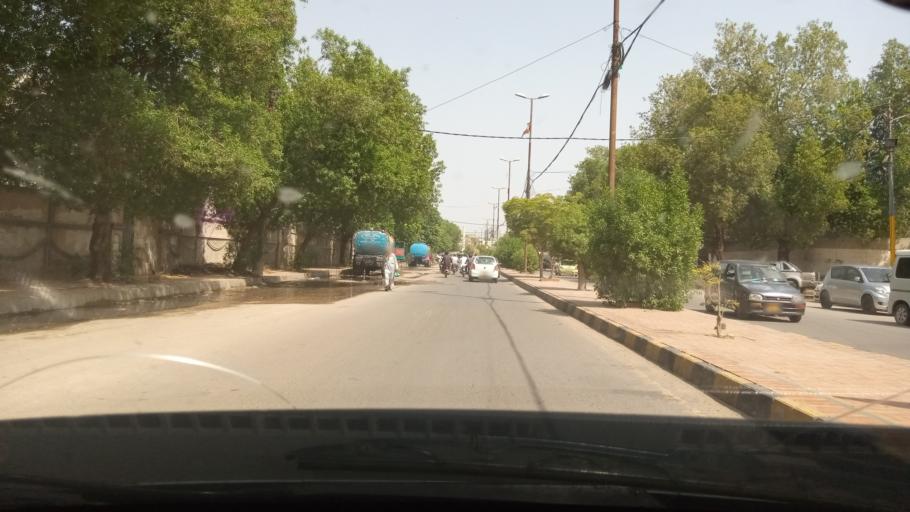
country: PK
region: Sindh
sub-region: Karachi District
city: Karachi
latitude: 24.8750
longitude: 67.0462
